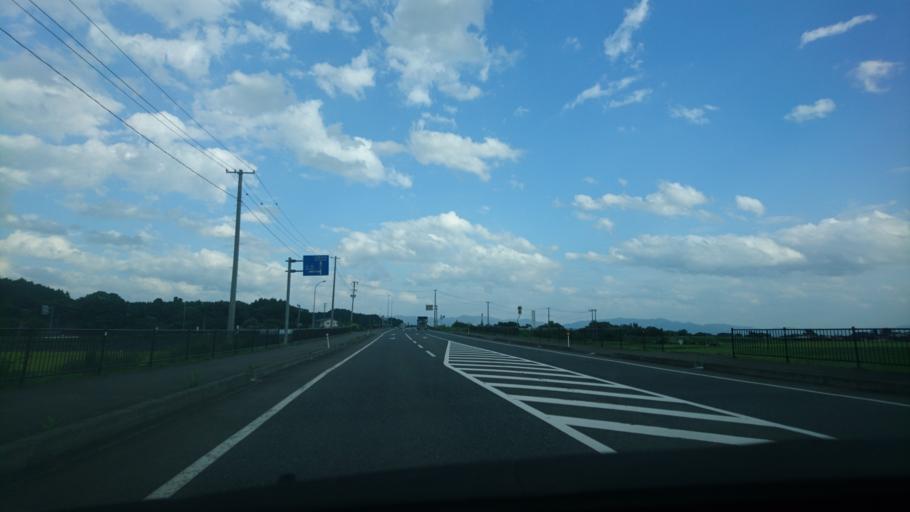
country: JP
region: Iwate
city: Mizusawa
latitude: 39.2069
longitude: 141.1568
